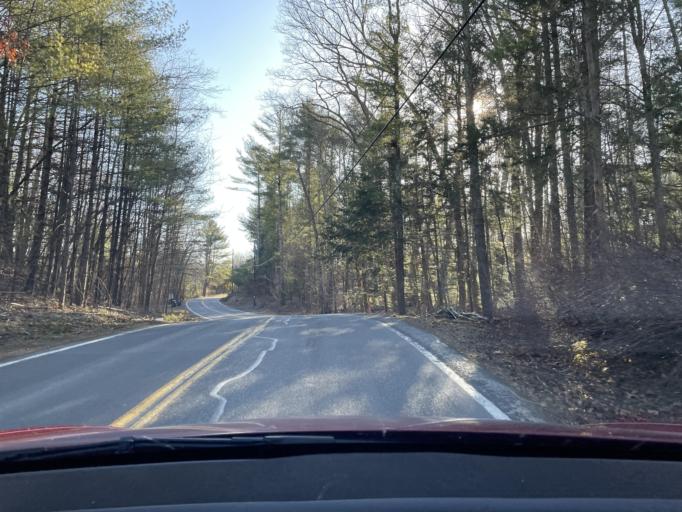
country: US
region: New York
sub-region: Ulster County
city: Zena
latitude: 42.0461
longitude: -74.0417
